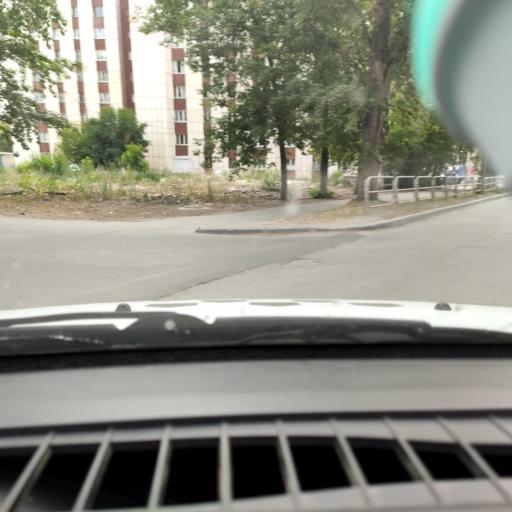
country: RU
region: Chelyabinsk
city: Miass
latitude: 55.0641
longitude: 60.1110
